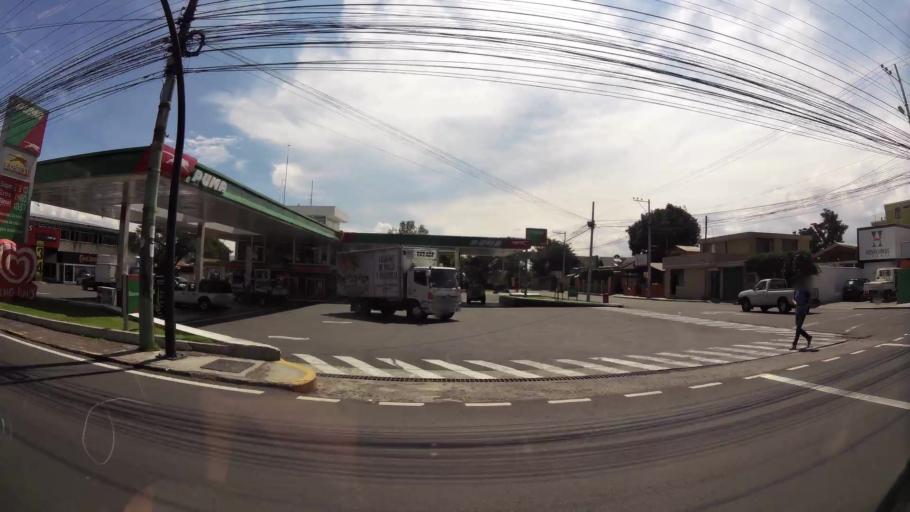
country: EC
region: Pichincha
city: Quito
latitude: -0.2111
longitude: -78.4142
